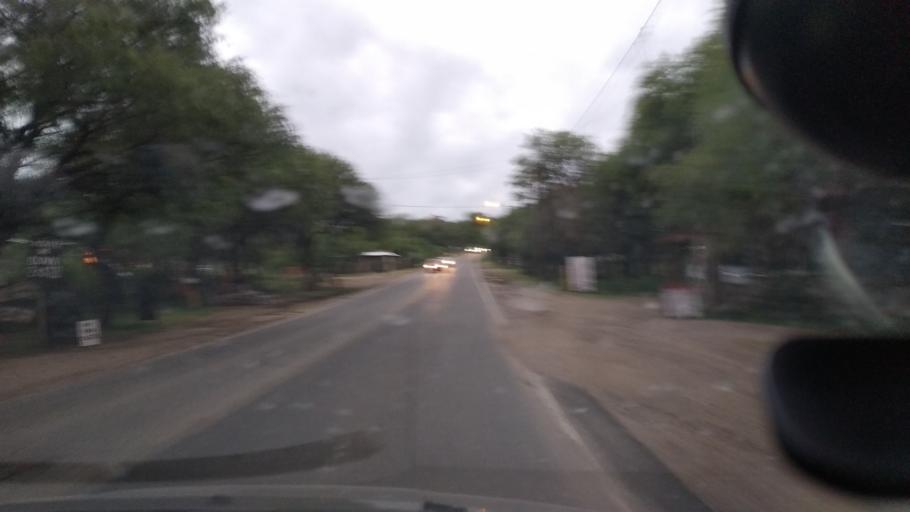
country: AR
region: Cordoba
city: Villa Las Rosas
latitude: -31.9267
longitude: -65.0393
